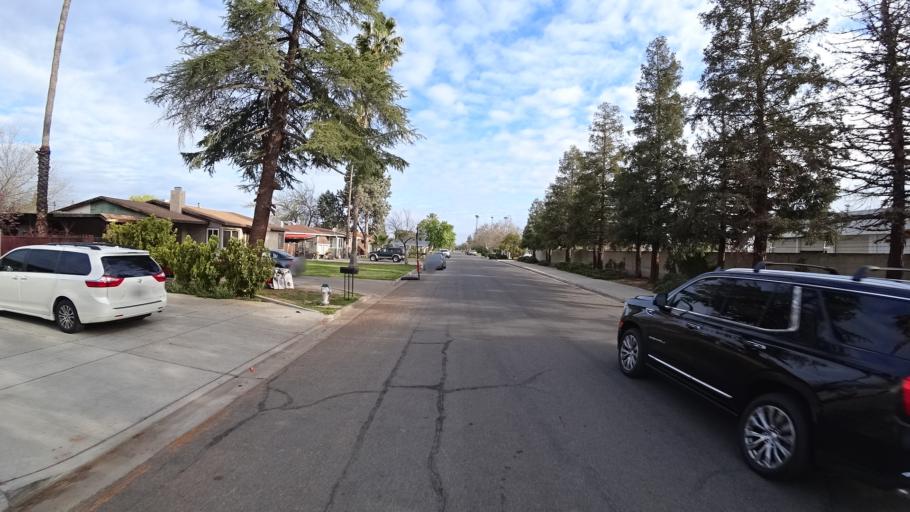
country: US
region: California
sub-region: Fresno County
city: Fresno
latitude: 36.8247
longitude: -119.7926
